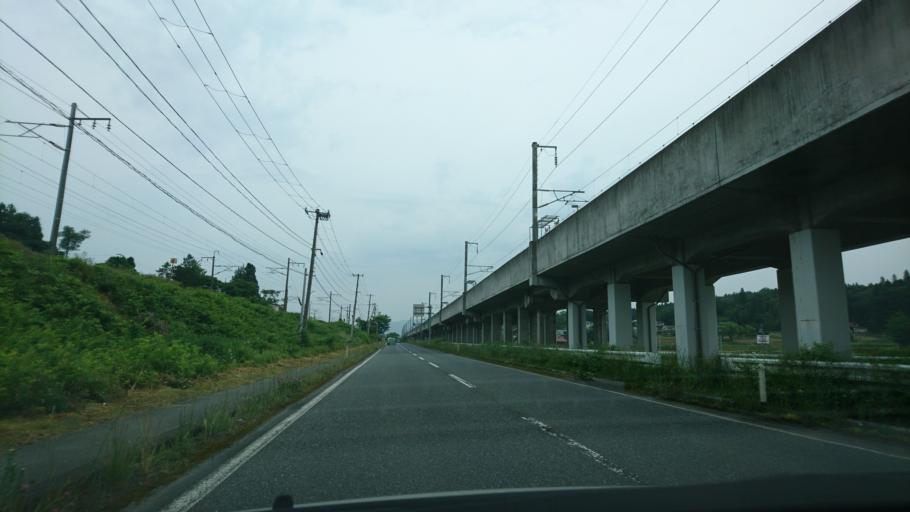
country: JP
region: Iwate
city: Ichinoseki
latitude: 38.9025
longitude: 141.1298
